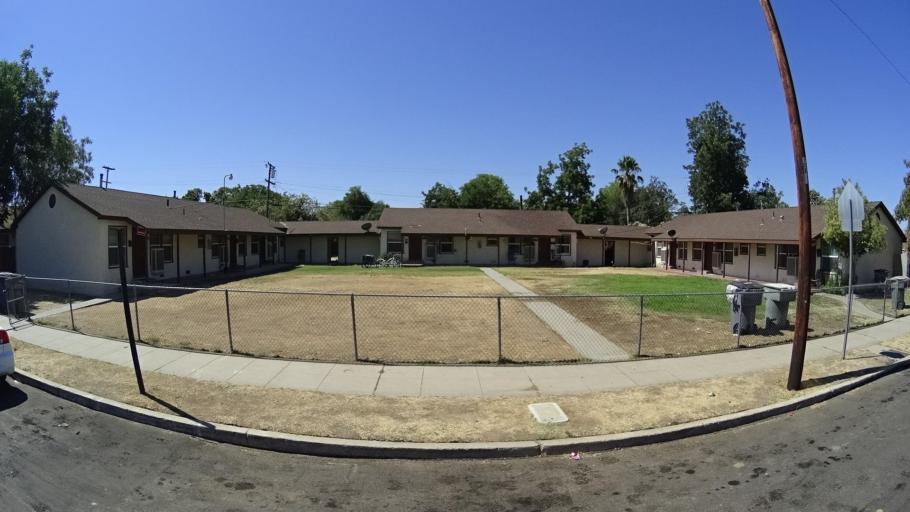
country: US
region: California
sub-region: Fresno County
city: Fresno
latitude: 36.7559
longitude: -119.7936
